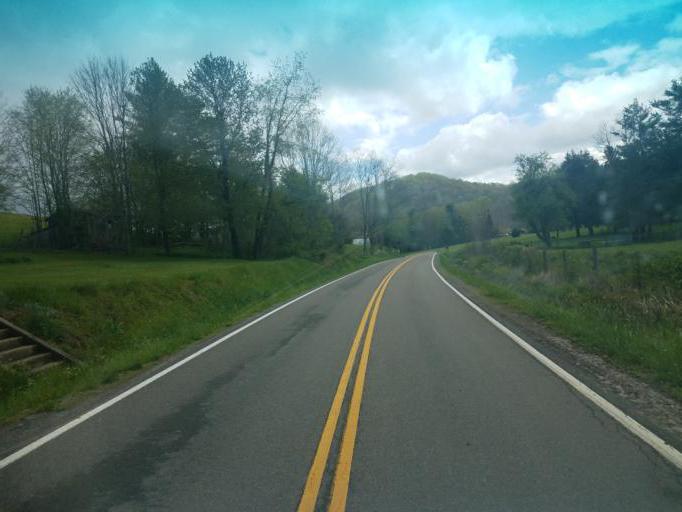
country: US
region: Virginia
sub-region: Wythe County
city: Rural Retreat
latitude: 37.0174
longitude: -81.3479
